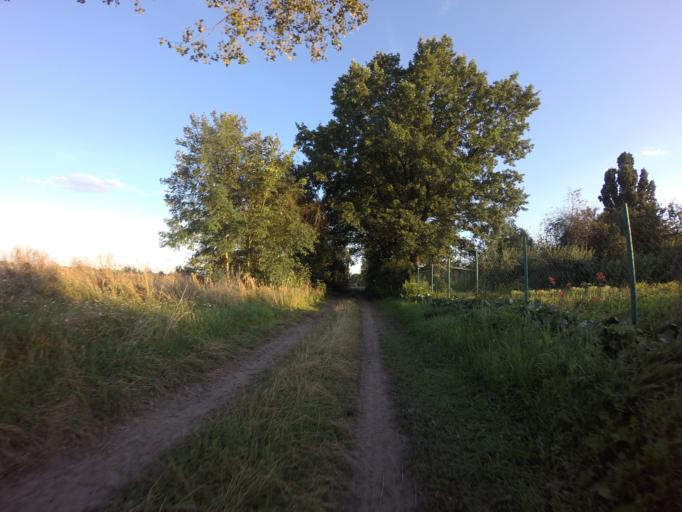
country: PL
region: West Pomeranian Voivodeship
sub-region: Powiat choszczenski
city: Choszczno
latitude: 53.1884
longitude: 15.4170
